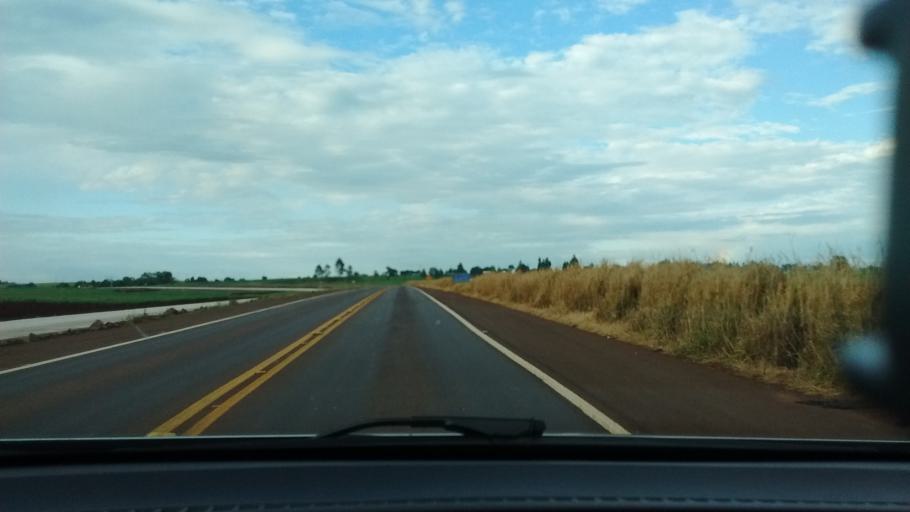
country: BR
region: Parana
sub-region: Cascavel
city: Cascavel
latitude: -25.0365
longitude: -53.5540
